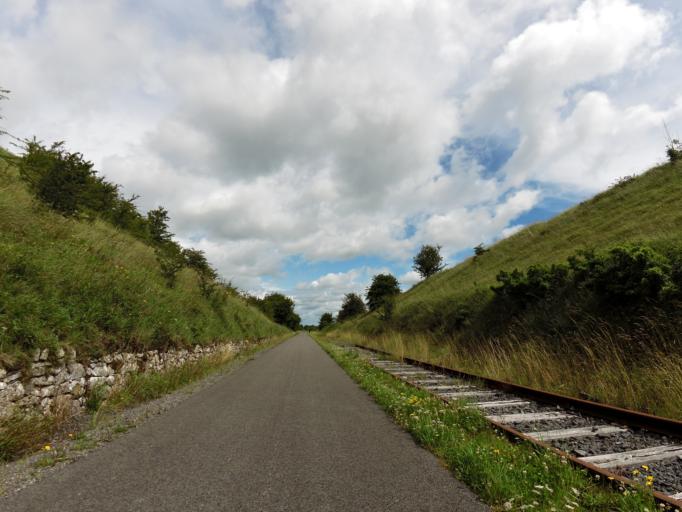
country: IE
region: Leinster
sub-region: An Iarmhi
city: Kilbeggan
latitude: 53.4676
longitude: -7.4979
